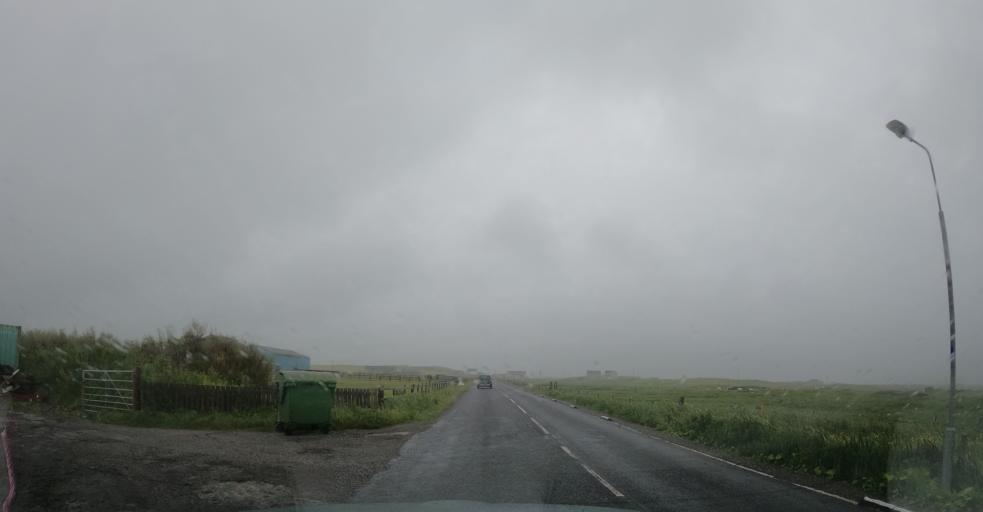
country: GB
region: Scotland
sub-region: Eilean Siar
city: Benbecula
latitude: 57.4718
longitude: -7.3667
